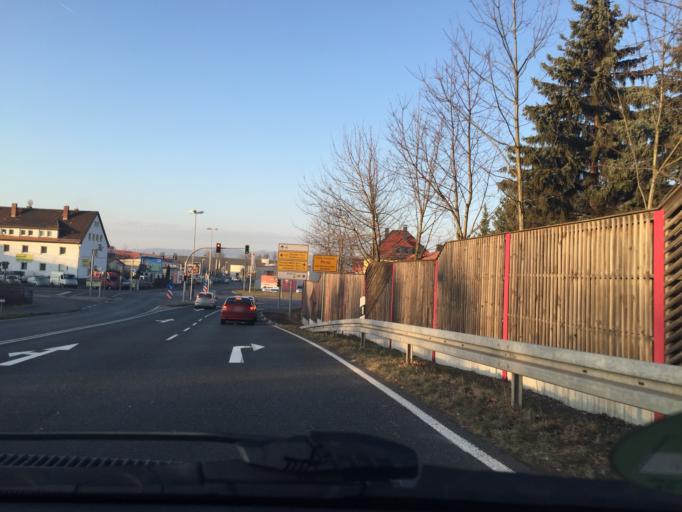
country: DE
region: Saxony
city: Pirna
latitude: 50.9565
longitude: 13.9194
